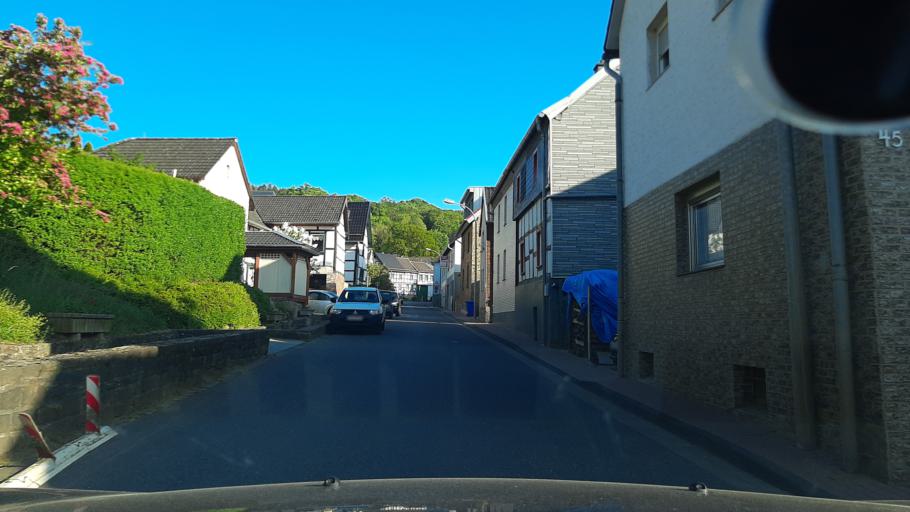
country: DE
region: North Rhine-Westphalia
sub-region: Regierungsbezirk Koln
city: Mechernich
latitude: 50.5523
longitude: 6.6592
